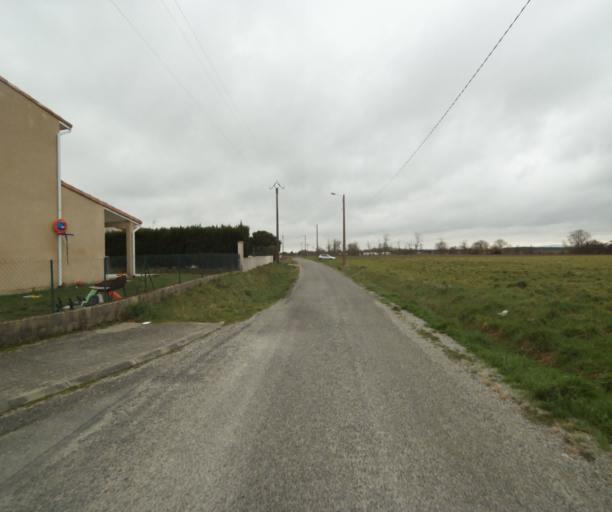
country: FR
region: Midi-Pyrenees
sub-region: Departement de l'Ariege
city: Mazeres
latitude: 43.2404
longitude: 1.6799
